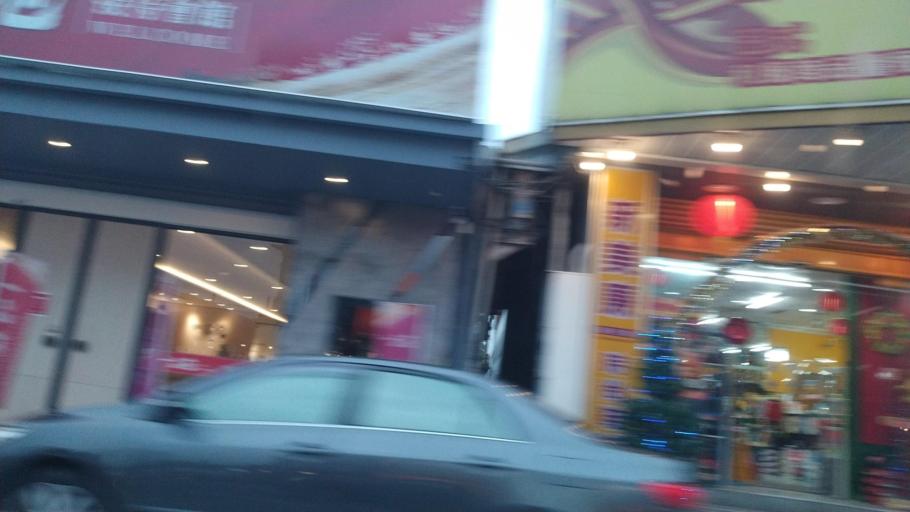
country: TW
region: Taiwan
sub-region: Hualien
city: Hualian
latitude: 23.9737
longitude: 121.5782
